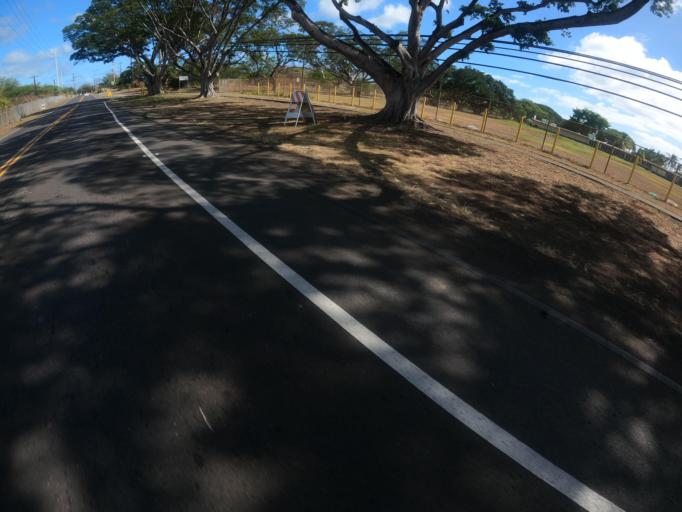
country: US
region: Hawaii
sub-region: Honolulu County
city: Makakilo City
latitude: 21.3238
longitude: -158.0811
